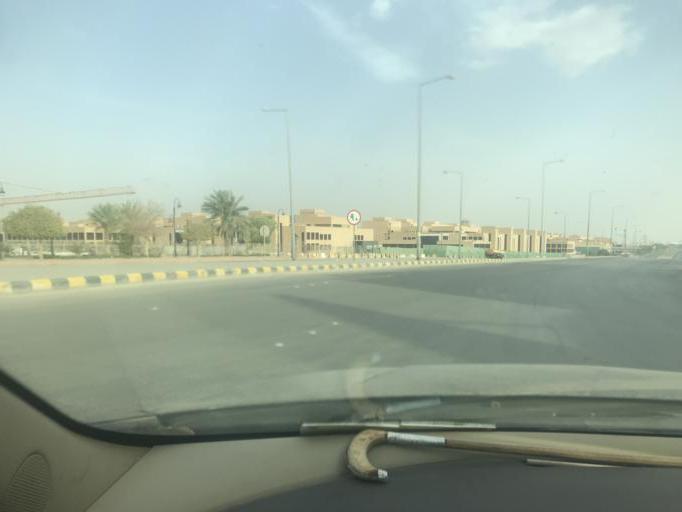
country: SA
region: Ar Riyad
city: Riyadh
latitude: 24.8174
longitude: 46.6877
